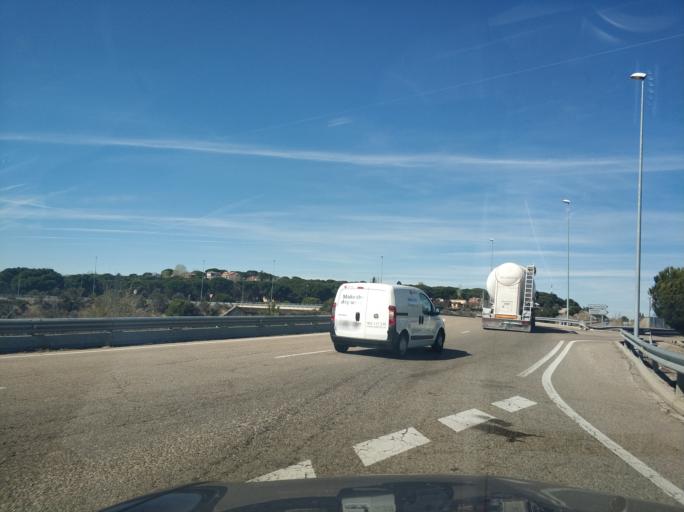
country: ES
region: Castille and Leon
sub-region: Provincia de Valladolid
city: Boecillo
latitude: 41.5484
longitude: -4.6615
